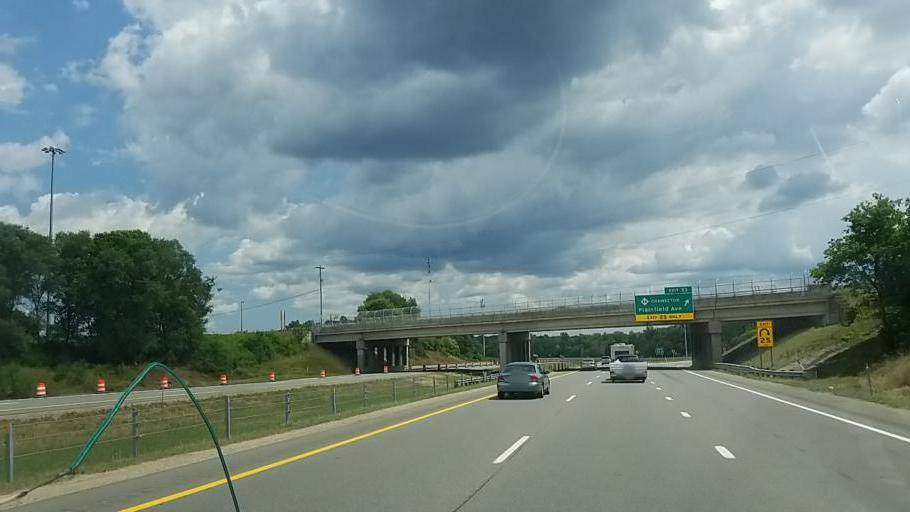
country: US
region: Michigan
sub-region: Kent County
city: Comstock Park
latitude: 43.0198
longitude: -85.6376
